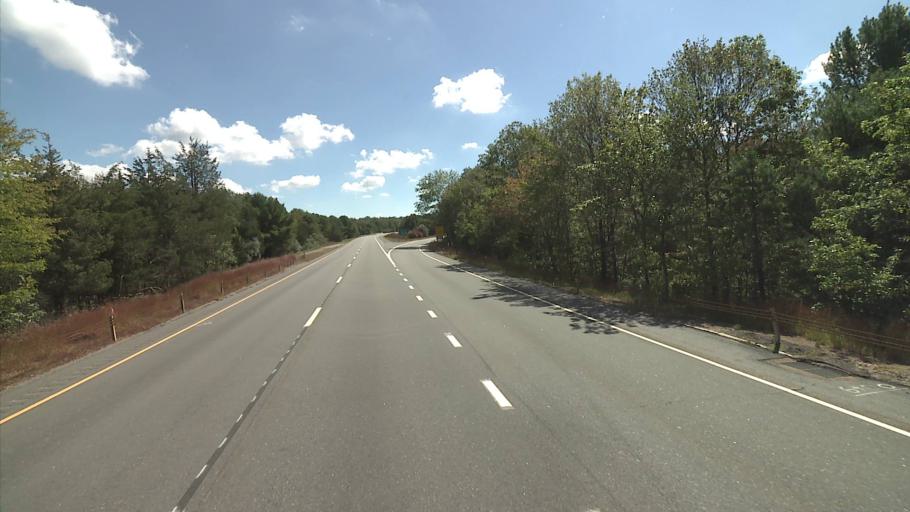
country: US
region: Connecticut
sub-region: New London County
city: Colchester
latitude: 41.5613
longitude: -72.3256
